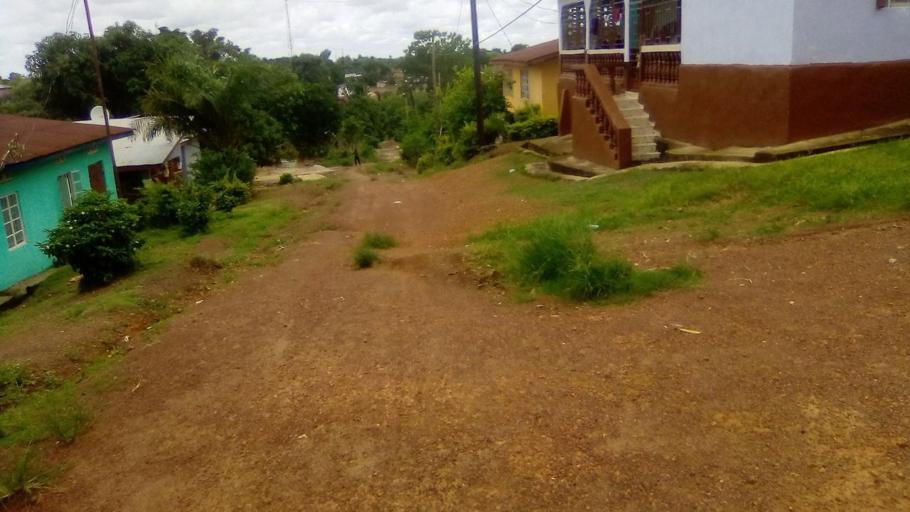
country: SL
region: Southern Province
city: Bo
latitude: 7.9437
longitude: -11.7433
